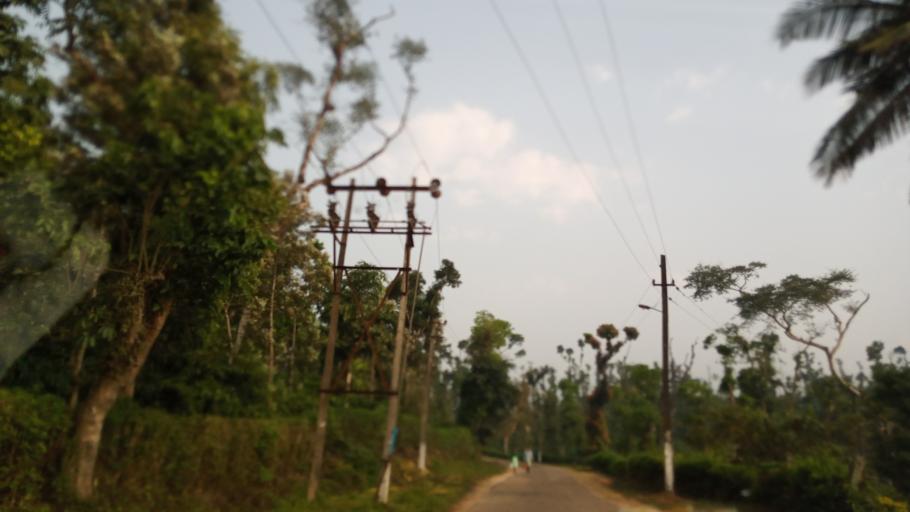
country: IN
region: Karnataka
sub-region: Chikmagalur
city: Mudigere
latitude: 13.0215
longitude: 75.6314
